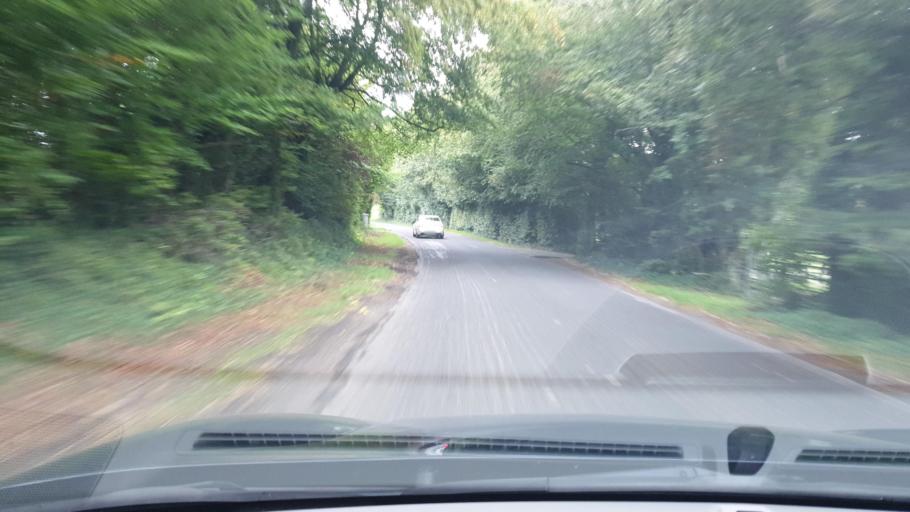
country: IE
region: Leinster
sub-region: An Mhi
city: Dunshaughlin
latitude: 53.5364
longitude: -6.5396
